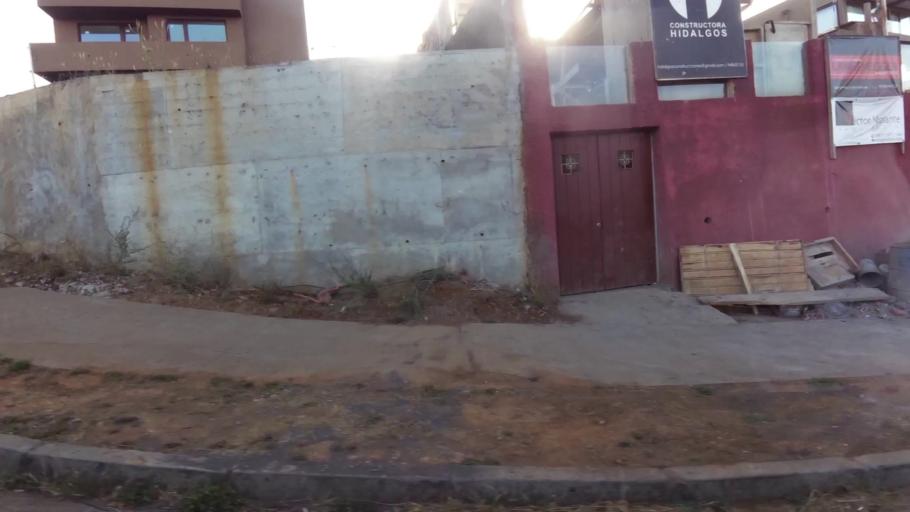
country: CL
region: Biobio
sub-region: Provincia de Concepcion
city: Concepcion
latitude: -36.8529
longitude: -73.0904
